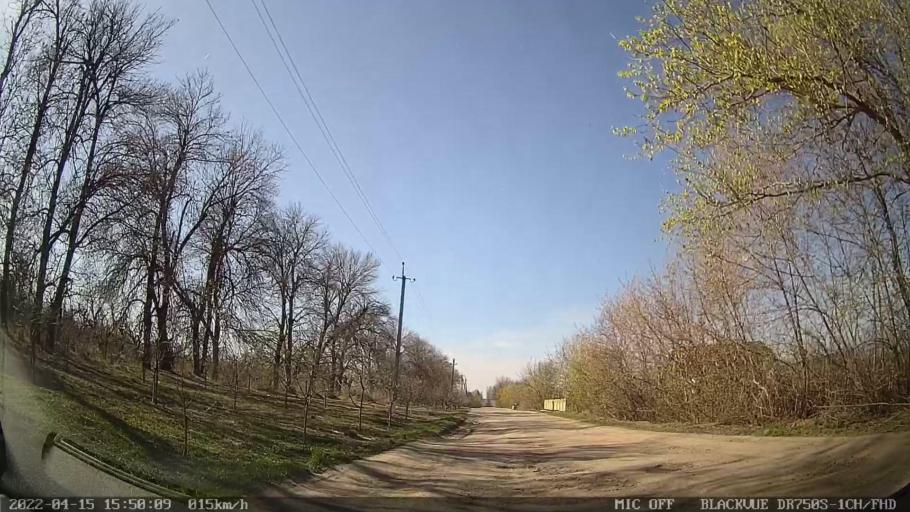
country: MD
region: Raionul Ocnita
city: Otaci
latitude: 48.3911
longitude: 27.9018
